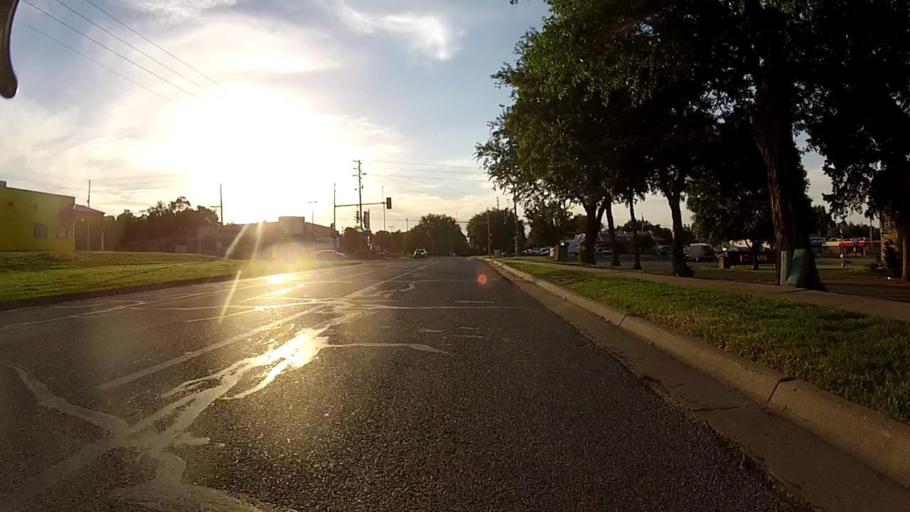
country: US
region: Kansas
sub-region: Cowley County
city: Arkansas City
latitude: 37.0854
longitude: -97.0409
